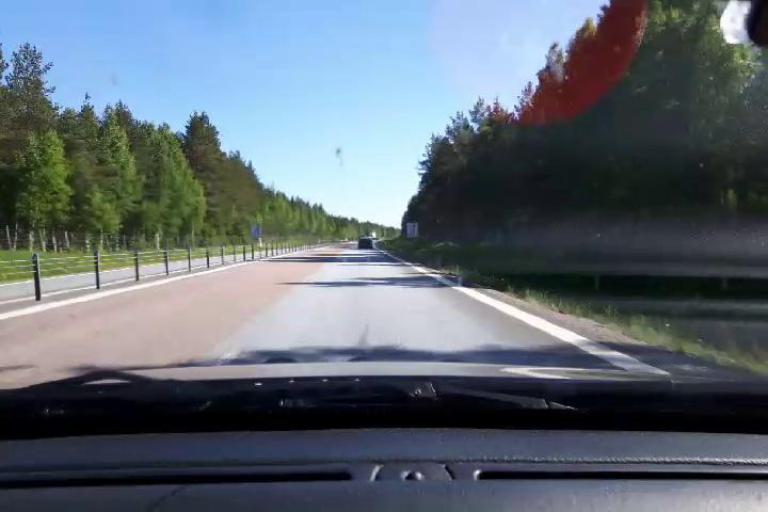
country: SE
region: Gaevleborg
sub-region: Gavle Kommun
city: Norrsundet
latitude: 60.8319
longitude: 17.0815
